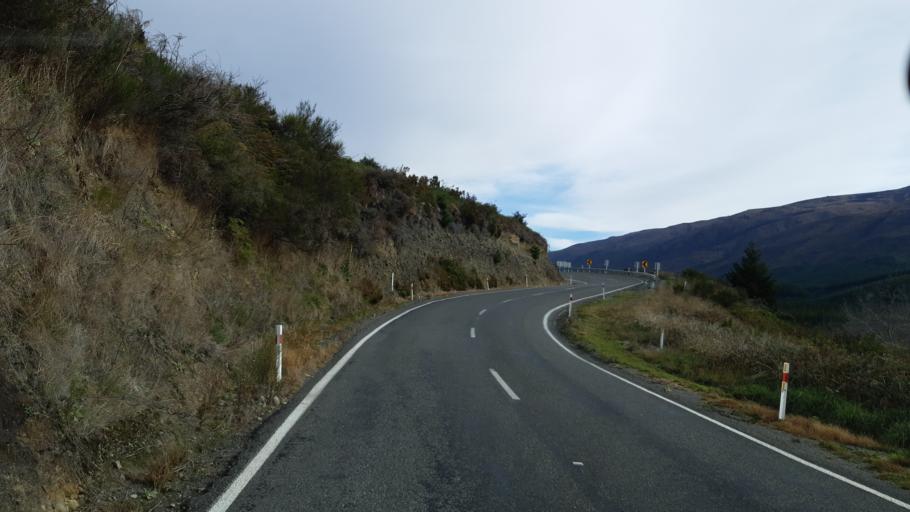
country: NZ
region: Tasman
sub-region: Tasman District
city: Wakefield
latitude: -41.6960
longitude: 173.1353
